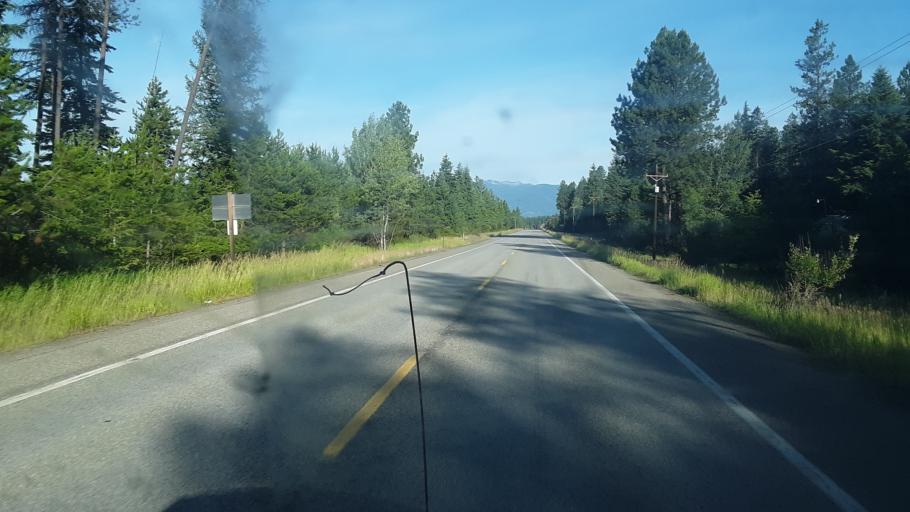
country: US
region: Idaho
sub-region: Boundary County
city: Bonners Ferry
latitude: 48.7272
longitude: -116.2157
